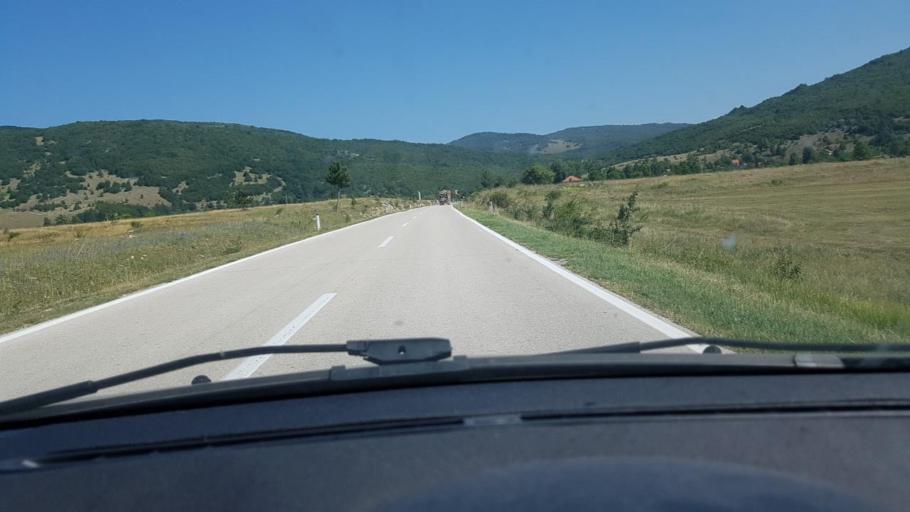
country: BA
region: Federation of Bosnia and Herzegovina
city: Bosansko Grahovo
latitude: 44.2885
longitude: 16.3027
